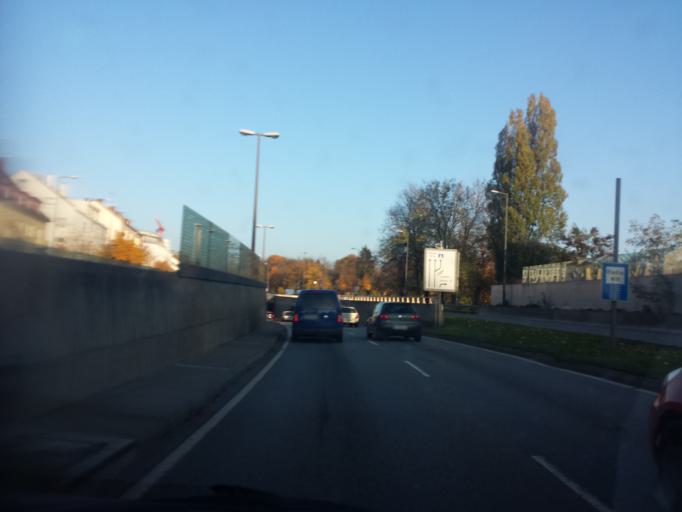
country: DE
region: Bavaria
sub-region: Upper Bavaria
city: Munich
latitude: 48.1760
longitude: 11.5654
